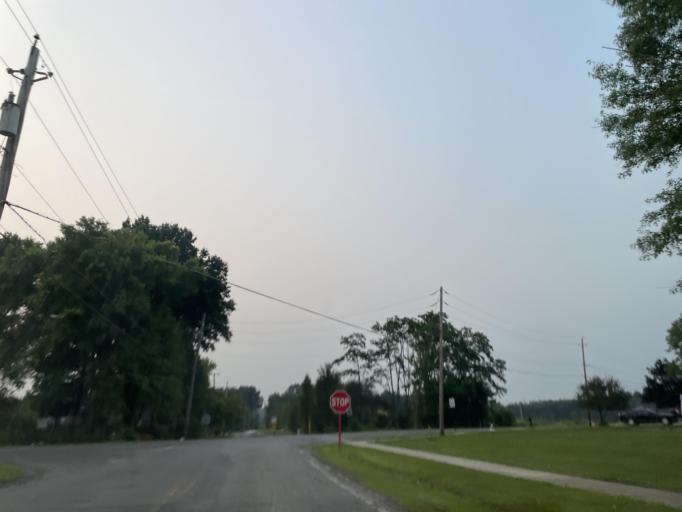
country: US
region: Ohio
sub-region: Trumbull County
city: McDonald
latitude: 41.1657
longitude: -80.7329
